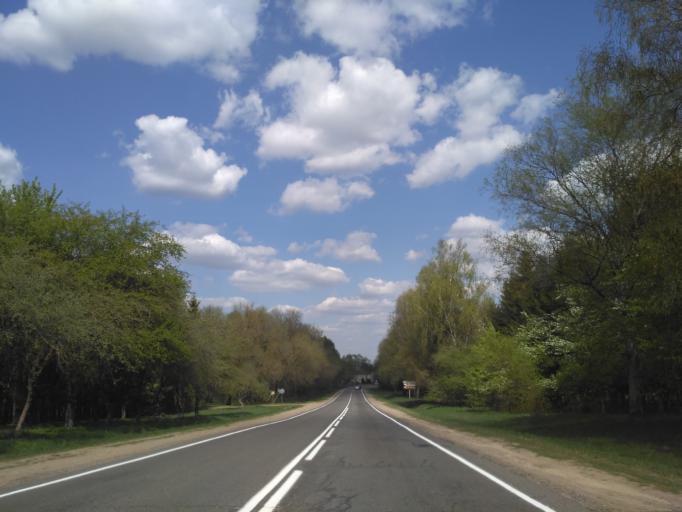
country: BY
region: Minsk
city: Vilyeyka
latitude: 54.5893
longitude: 26.8746
